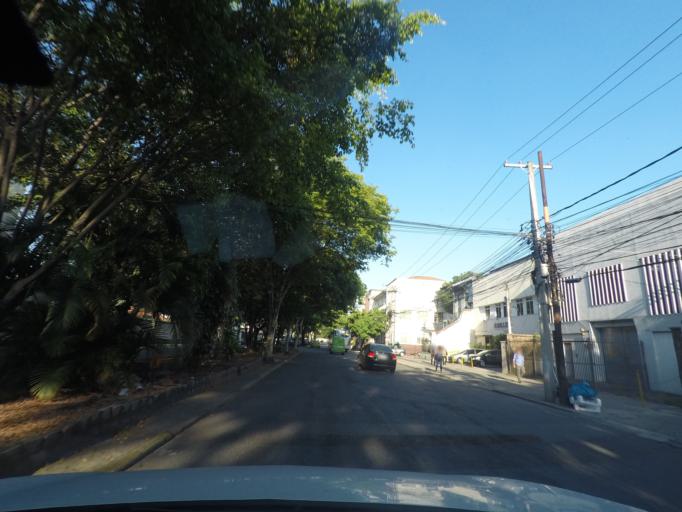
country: BR
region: Rio de Janeiro
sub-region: Rio De Janeiro
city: Rio de Janeiro
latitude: -22.9032
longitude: -43.2141
